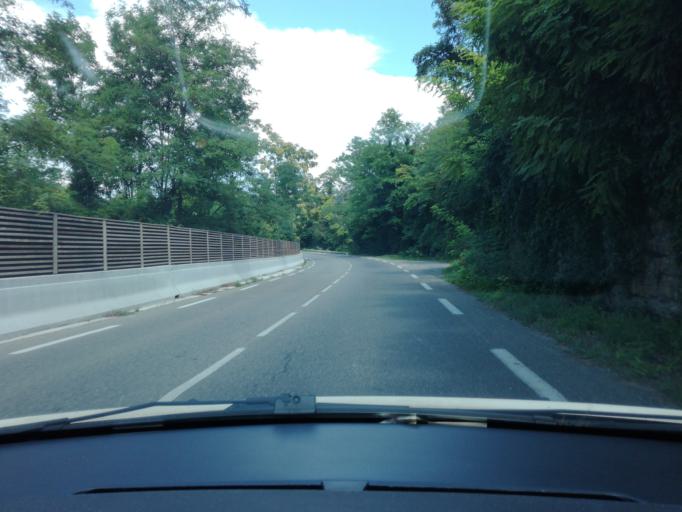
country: FR
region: Rhone-Alpes
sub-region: Departement de l'Ardeche
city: Ruoms
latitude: 44.4807
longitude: 4.3793
